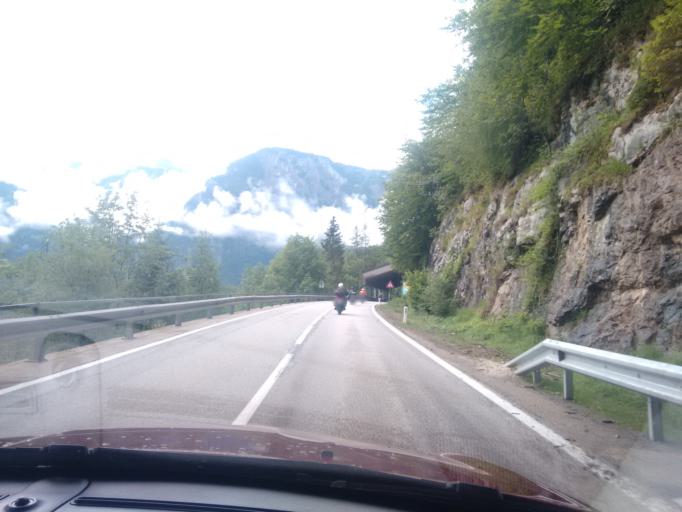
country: AT
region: Upper Austria
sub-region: Politischer Bezirk Gmunden
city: Bad Goisern
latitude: 47.5708
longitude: 13.6497
